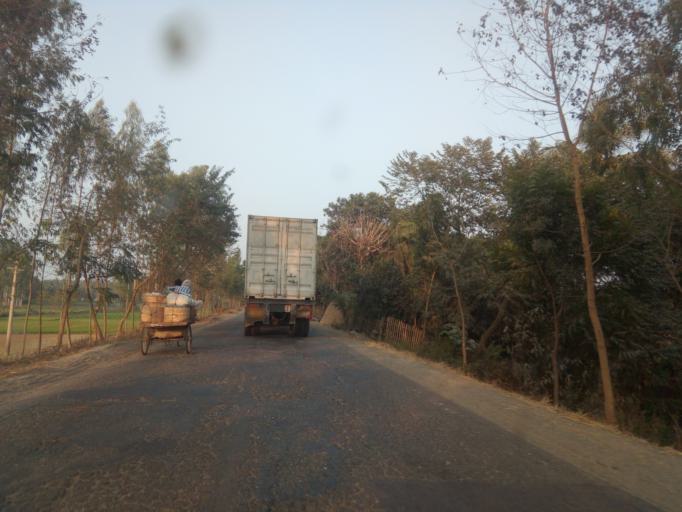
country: BD
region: Rajshahi
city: Par Naogaon
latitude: 24.5485
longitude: 89.1901
